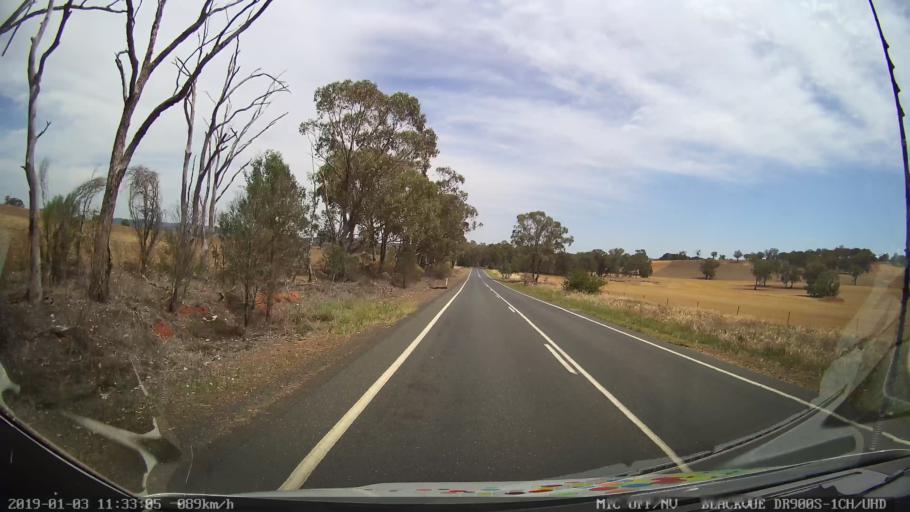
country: AU
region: New South Wales
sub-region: Weddin
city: Grenfell
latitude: -33.9506
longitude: 148.1742
